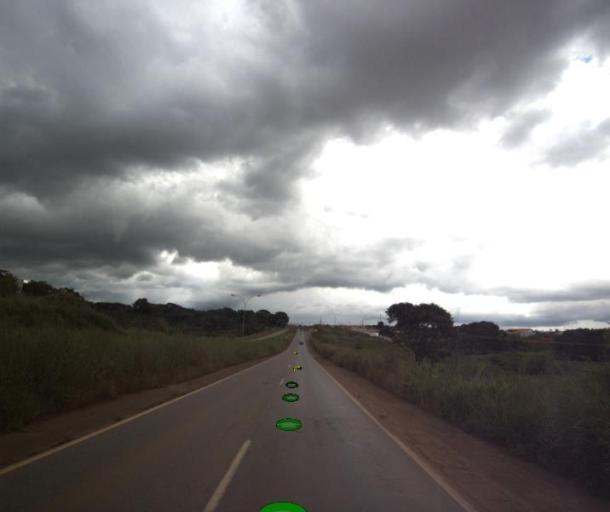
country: BR
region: Goias
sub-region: Anapolis
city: Anapolis
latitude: -16.2934
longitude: -48.9331
